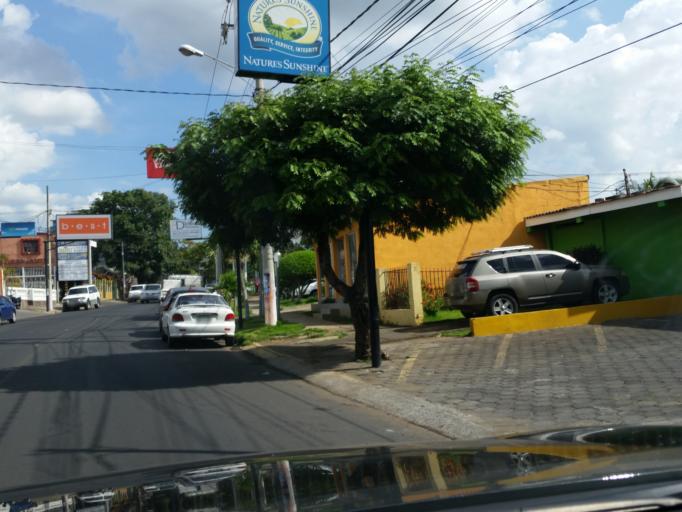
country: NI
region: Managua
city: Managua
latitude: 12.1273
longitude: -86.2617
